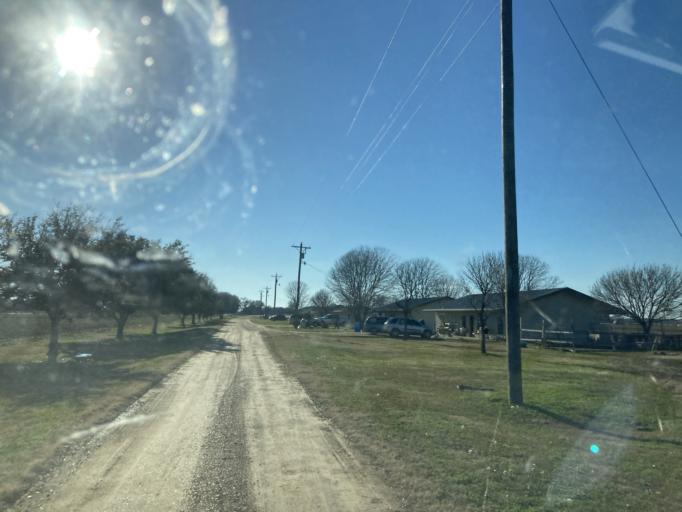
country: US
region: Mississippi
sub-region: Yazoo County
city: Yazoo City
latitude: 32.9248
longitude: -90.5068
